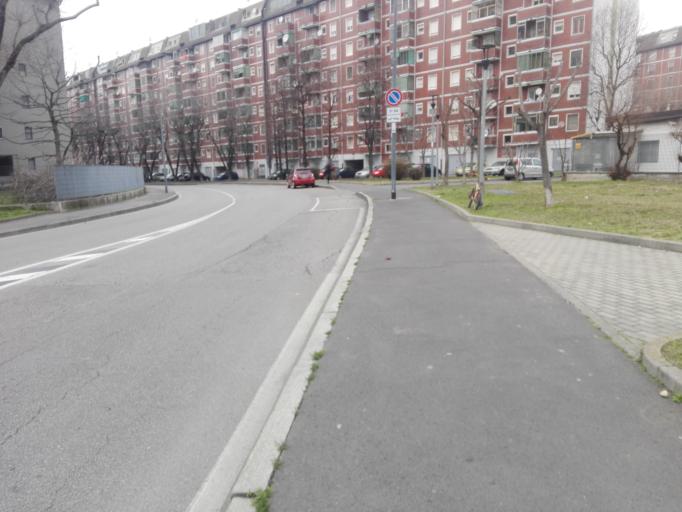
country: IT
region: Lombardy
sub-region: Citta metropolitana di Milano
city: Assago
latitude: 45.4292
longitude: 9.1586
